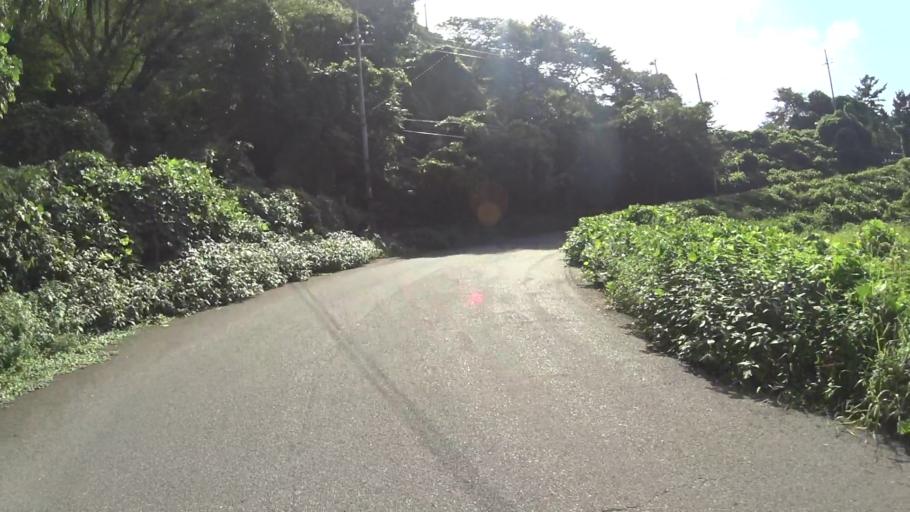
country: JP
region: Kyoto
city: Miyazu
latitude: 35.7698
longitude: 135.2217
